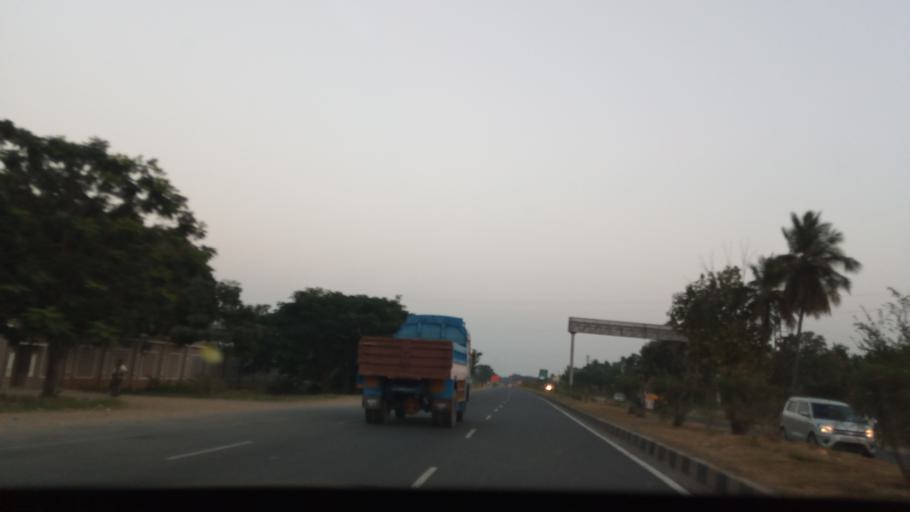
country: IN
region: Tamil Nadu
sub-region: Salem
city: Belur
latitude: 11.6605
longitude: 78.3323
